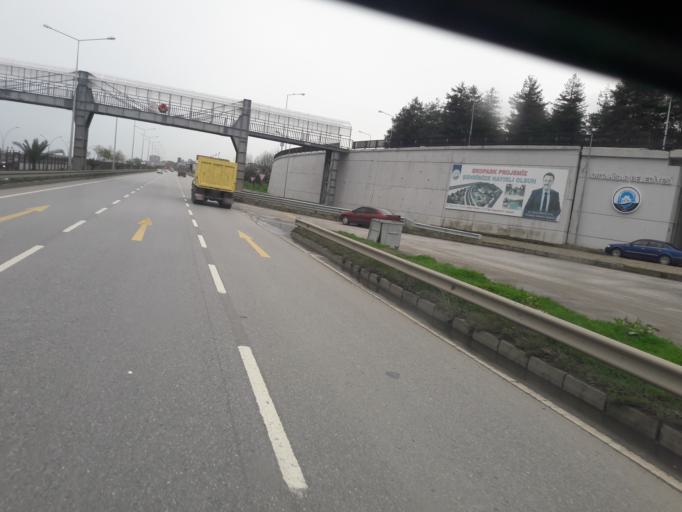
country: TR
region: Trabzon
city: Trabzon
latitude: 40.9981
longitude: 39.6745
